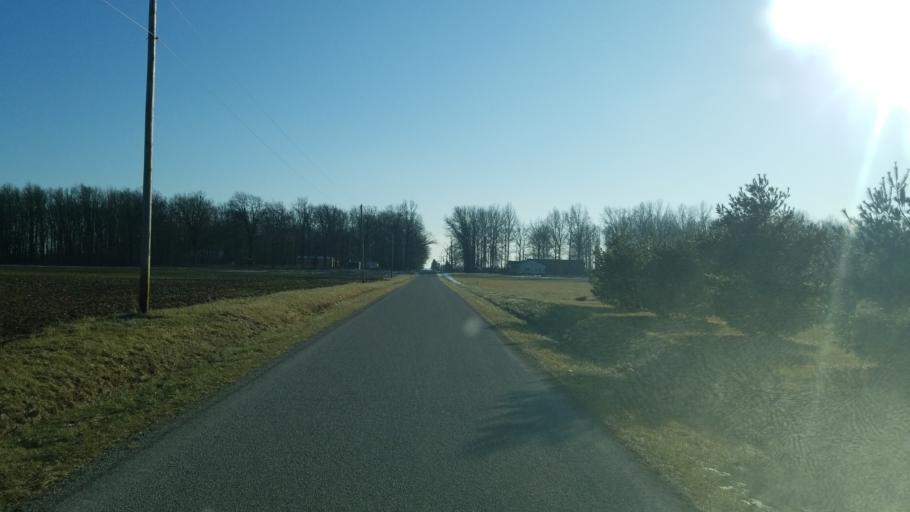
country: US
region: Ohio
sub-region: Sandusky County
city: Green Springs
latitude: 41.2094
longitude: -82.9950
